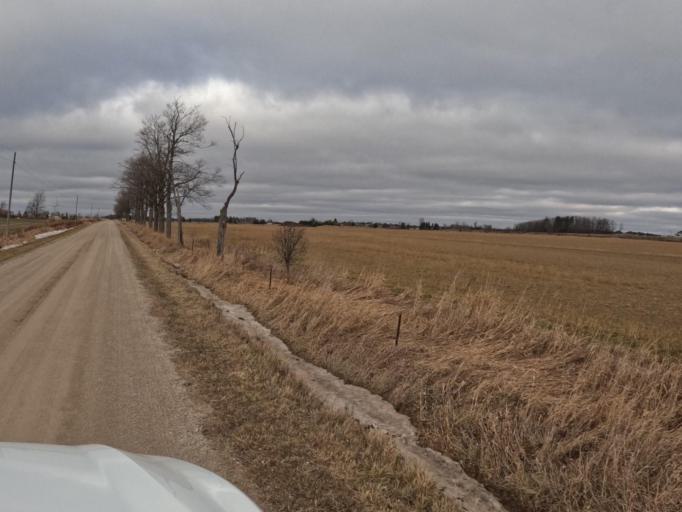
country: CA
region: Ontario
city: Shelburne
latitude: 43.8900
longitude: -80.3288
